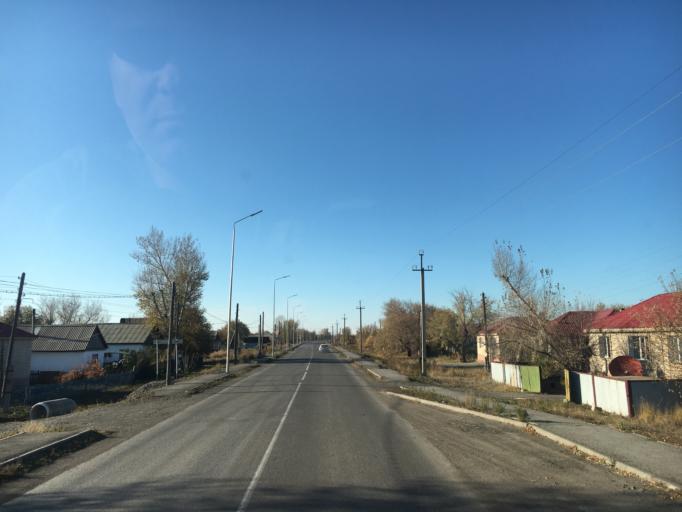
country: KZ
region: Qaraghandy
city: Tokarevka
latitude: 50.1362
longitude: 73.1810
